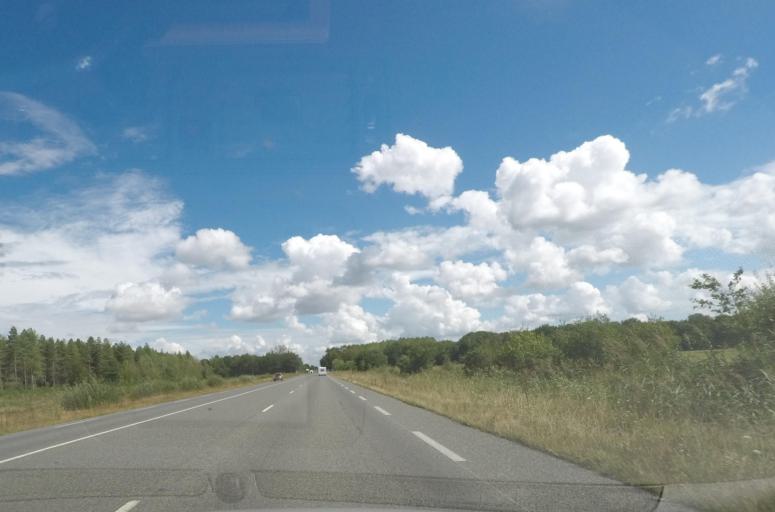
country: FR
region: Pays de la Loire
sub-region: Departement de la Sarthe
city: Parigne-le-Polin
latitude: 47.8631
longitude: 0.1106
